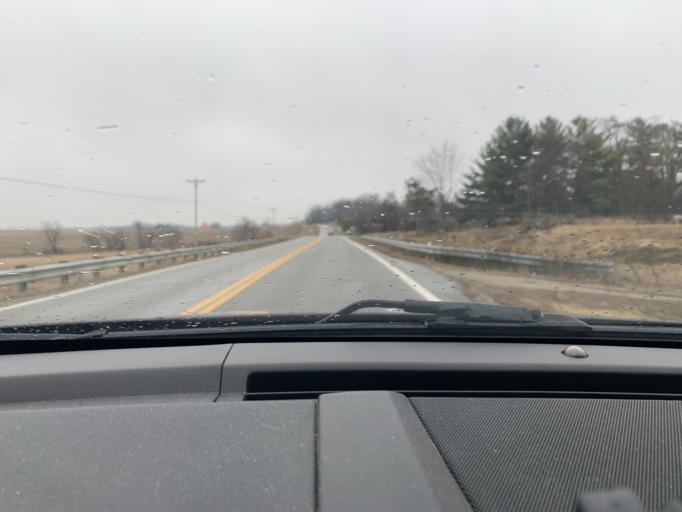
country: US
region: Ohio
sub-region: Ross County
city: Kingston
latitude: 39.4325
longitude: -82.9023
